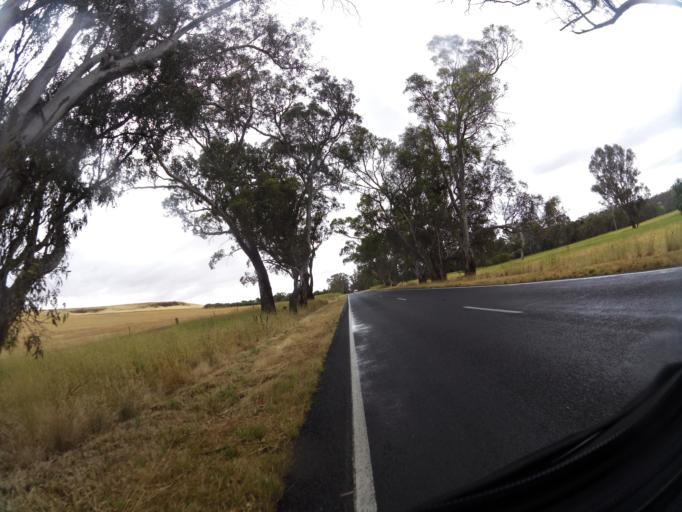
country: AU
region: Victoria
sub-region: Mount Alexander
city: Castlemaine
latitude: -37.1532
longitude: 144.0418
